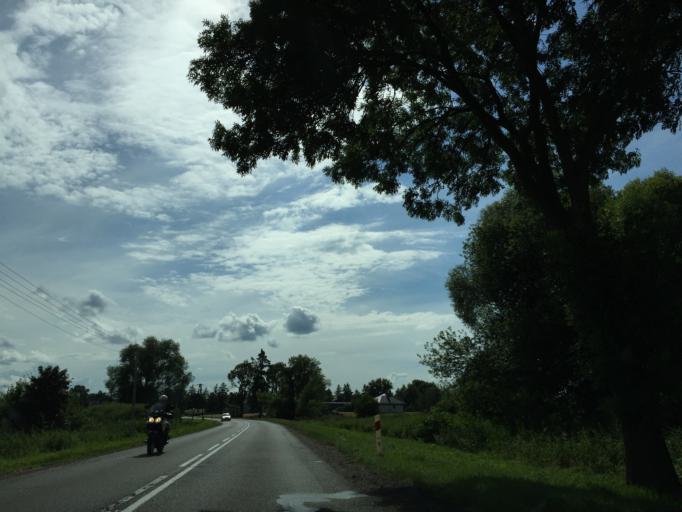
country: PL
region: Masovian Voivodeship
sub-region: Powiat losicki
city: Losice
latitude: 52.2441
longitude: 22.7794
